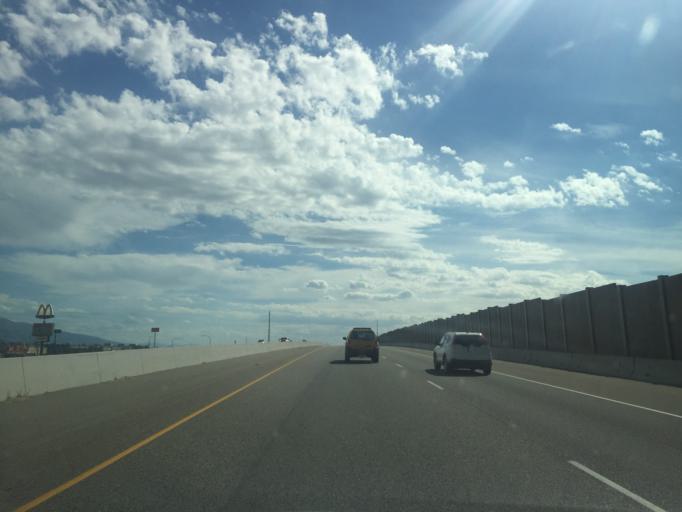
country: US
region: Utah
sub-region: Weber County
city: Farr West
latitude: 41.3094
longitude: -112.0261
